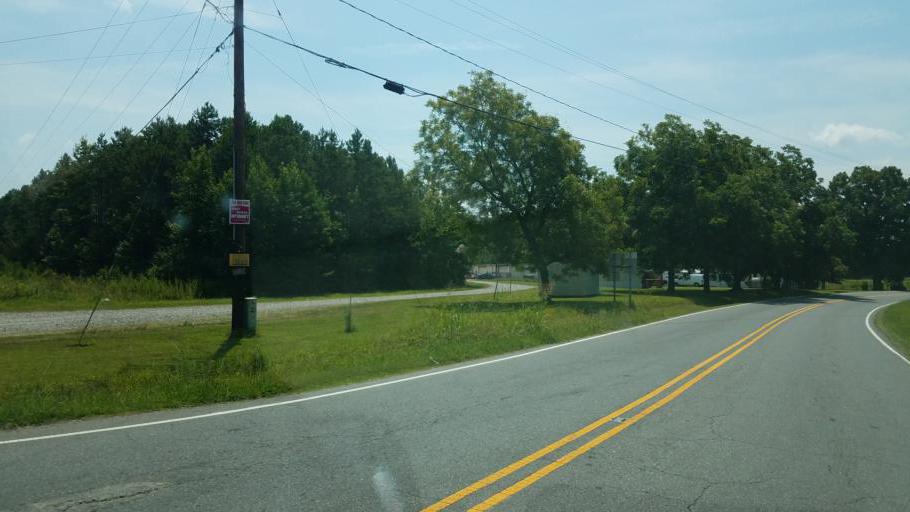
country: US
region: North Carolina
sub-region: Gaston County
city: Tryon
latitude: 35.3459
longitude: -81.3473
